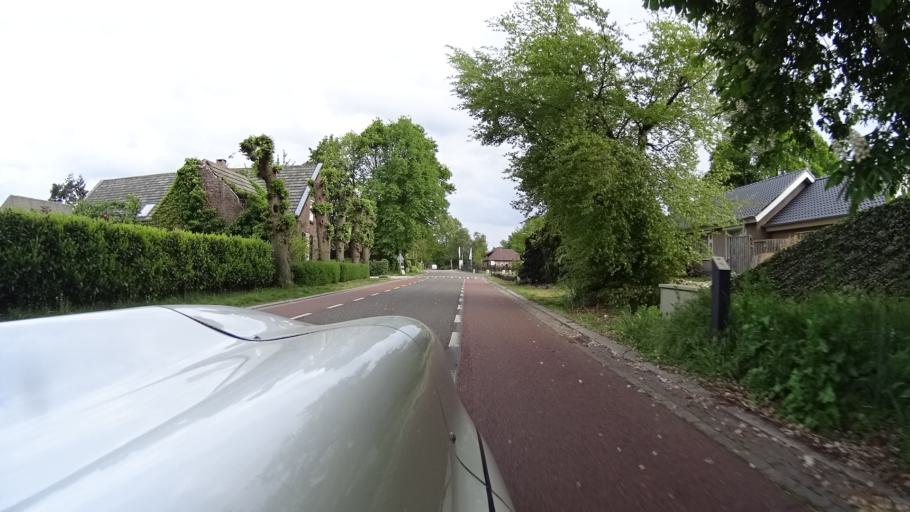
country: NL
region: North Brabant
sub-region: Gemeente Boekel
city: Boekel
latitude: 51.6171
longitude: 5.6786
